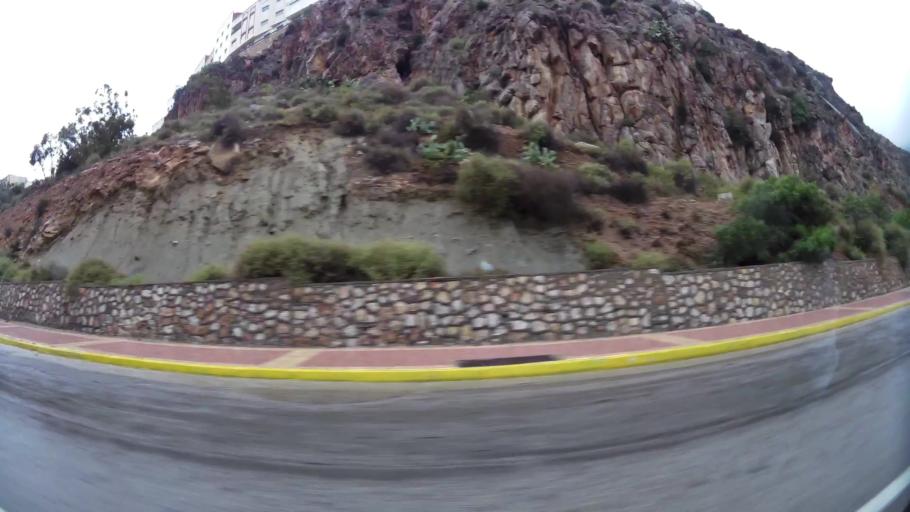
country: MA
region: Taza-Al Hoceima-Taounate
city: Al Hoceima
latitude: 35.2487
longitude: -3.9271
